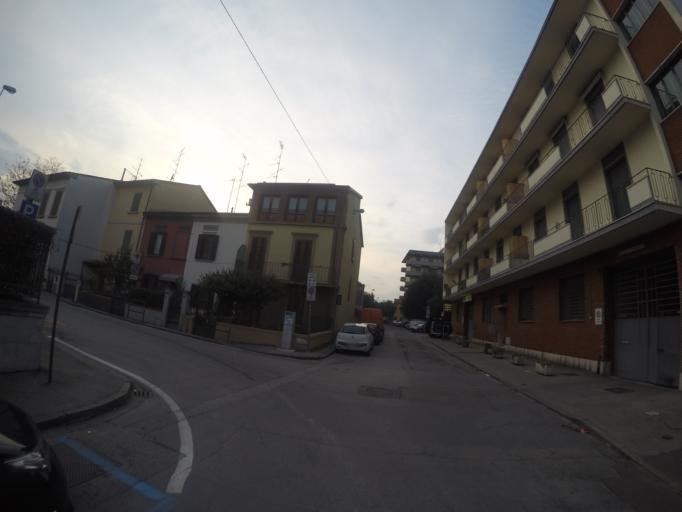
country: IT
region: Tuscany
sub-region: Provincia di Prato
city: Prato
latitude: 43.8851
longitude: 11.0926
